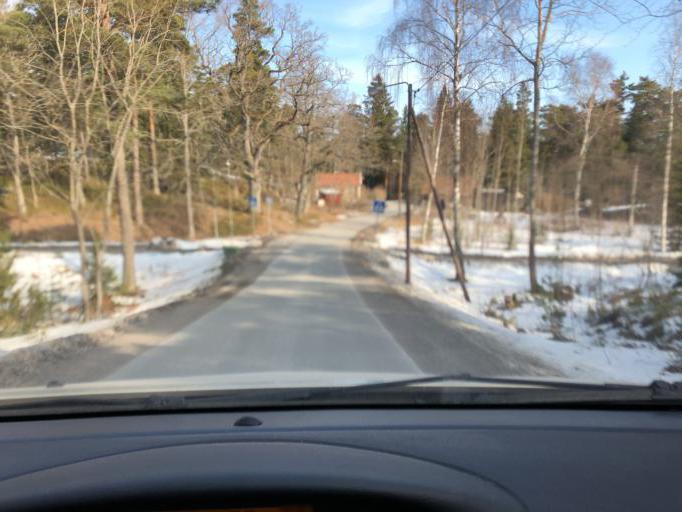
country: SE
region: Stockholm
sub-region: Nacka Kommun
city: Boo
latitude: 59.3406
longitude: 18.3184
